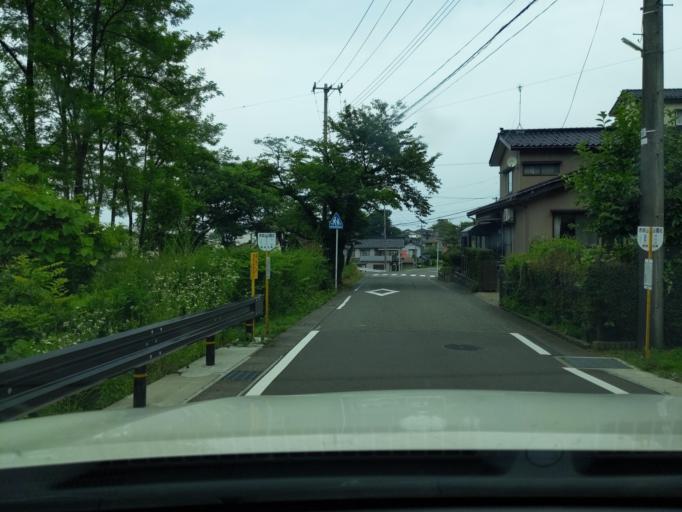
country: JP
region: Niigata
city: Kashiwazaki
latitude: 37.3606
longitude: 138.5395
